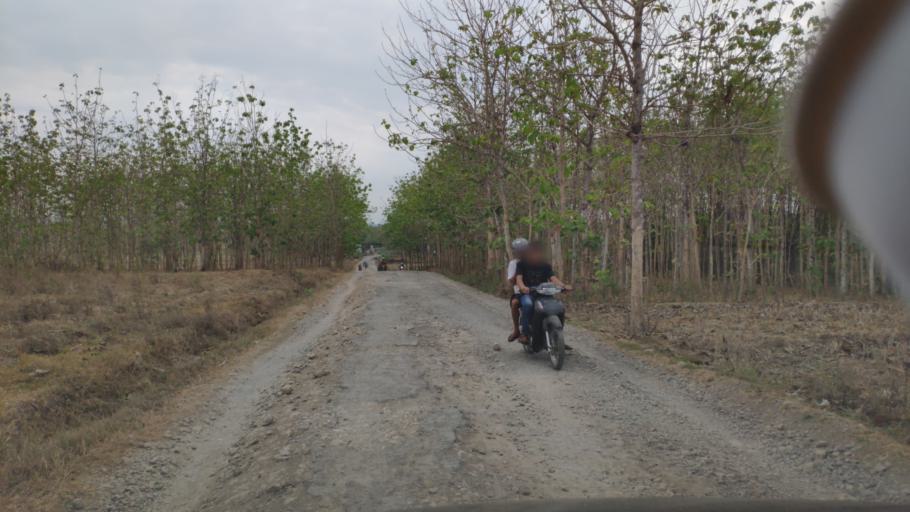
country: ID
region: Central Java
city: Jembangan
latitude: -6.9524
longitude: 111.3862
